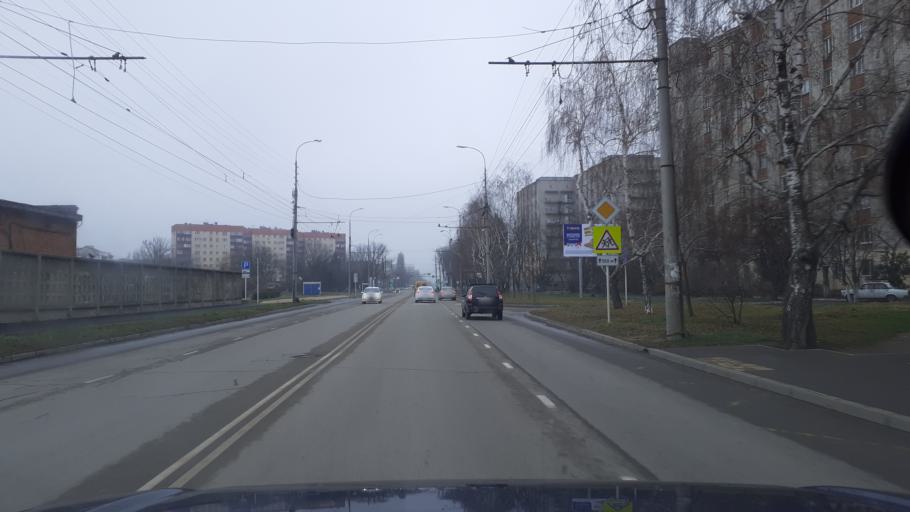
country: RU
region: Adygeya
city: Maykop
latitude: 44.6204
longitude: 40.0658
